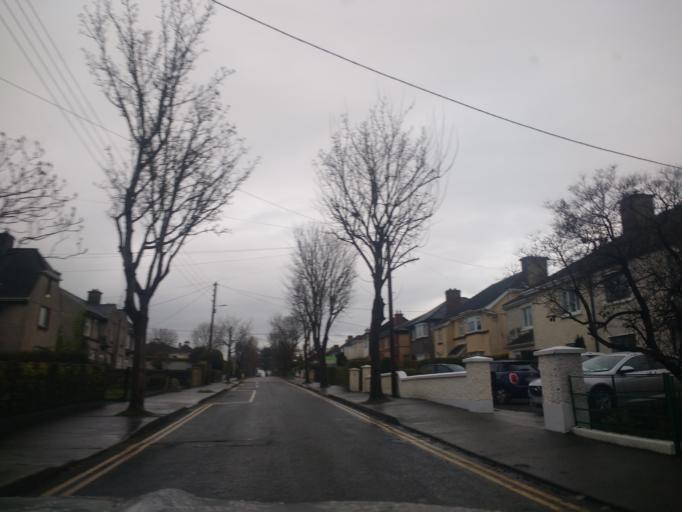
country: IE
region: Leinster
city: Malahide
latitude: 53.4479
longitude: -6.1560
